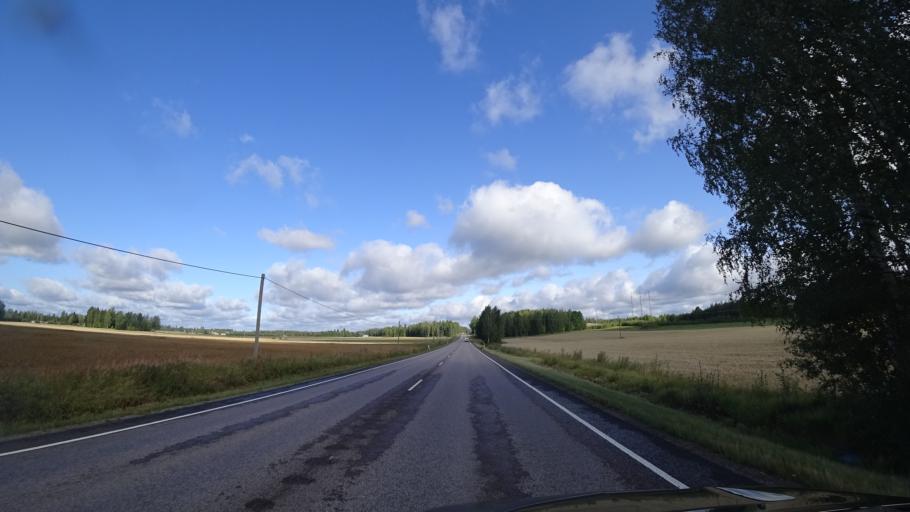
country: FI
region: Uusimaa
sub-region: Helsinki
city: Nurmijaervi
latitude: 60.5001
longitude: 24.9347
